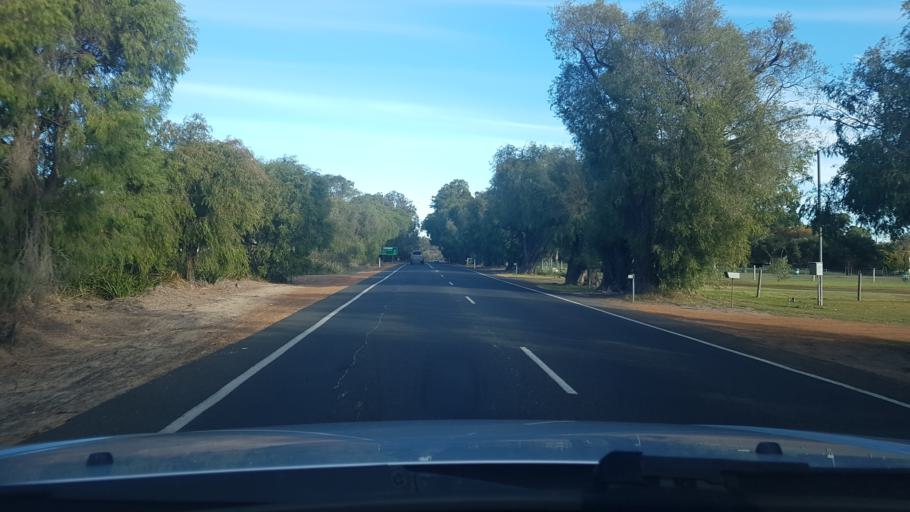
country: AU
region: Western Australia
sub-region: Busselton
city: Vasse
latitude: -33.6636
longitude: 115.2586
